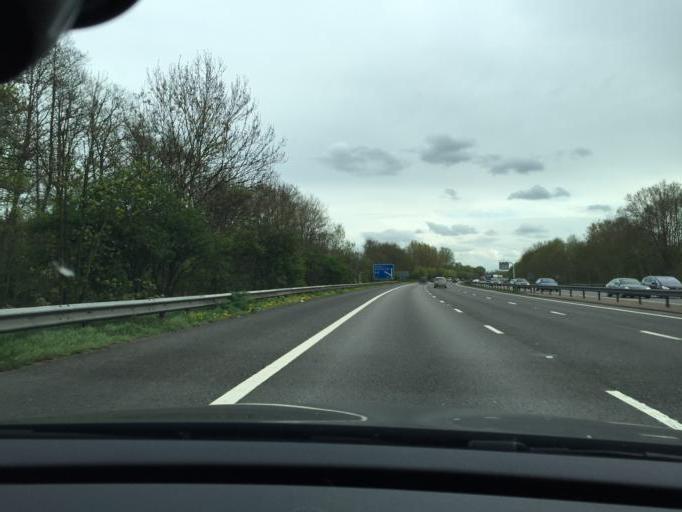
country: GB
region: England
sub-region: West Berkshire
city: Theale
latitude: 51.4509
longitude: -1.0770
